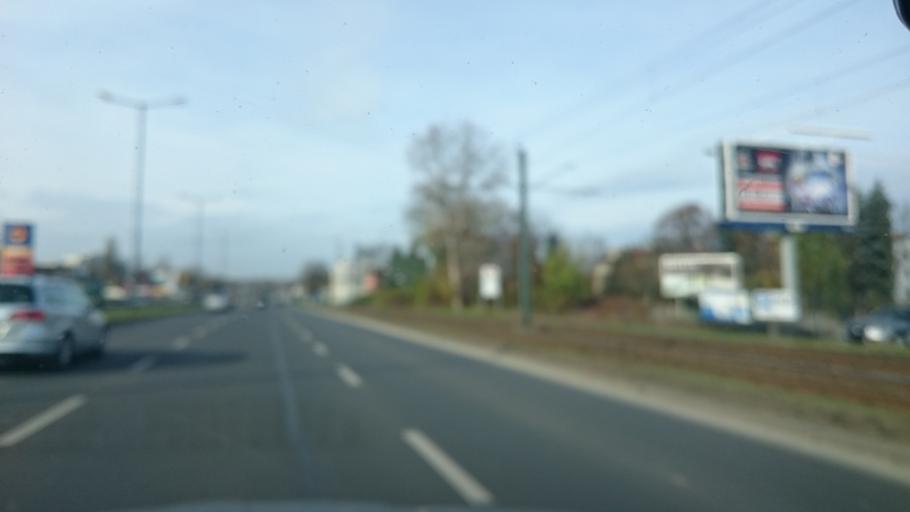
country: PL
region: Lesser Poland Voivodeship
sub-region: Krakow
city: Krakow
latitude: 50.0215
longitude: 19.9842
